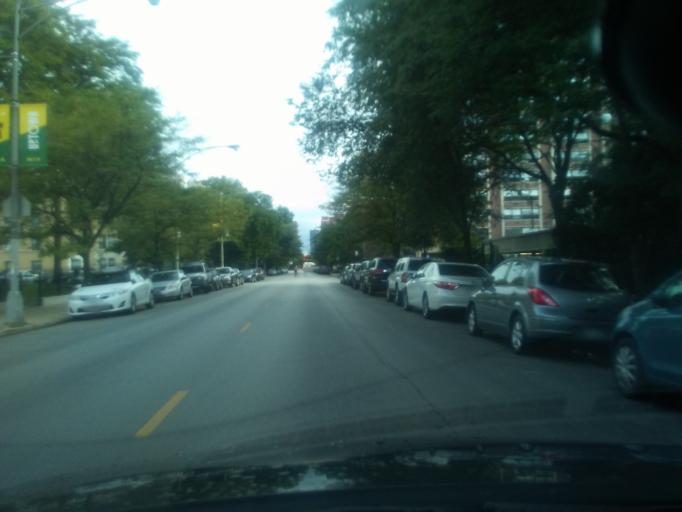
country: US
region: Illinois
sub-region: Cook County
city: Lincolnwood
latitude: 41.9588
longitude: -87.6547
